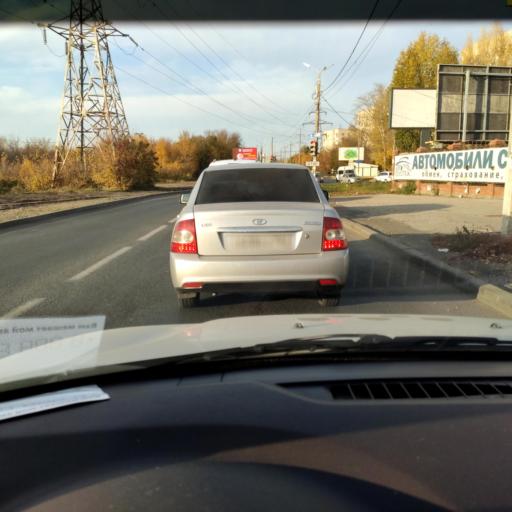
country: RU
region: Samara
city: Tol'yatti
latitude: 53.5239
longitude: 49.3960
